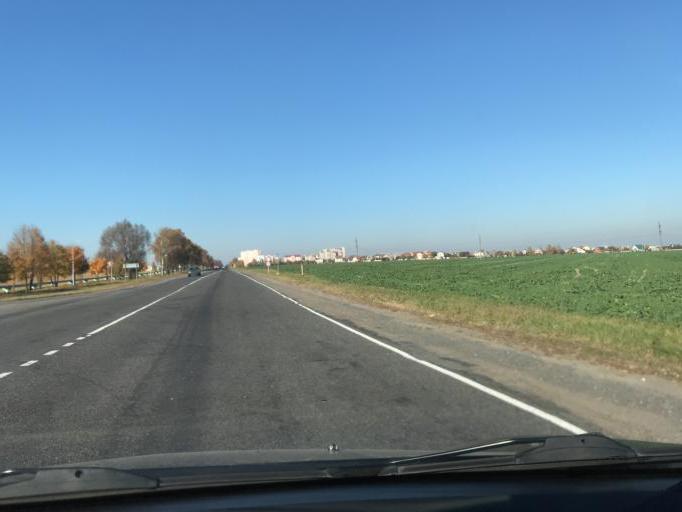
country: BY
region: Gomel
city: Kastsyukowka
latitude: 52.4557
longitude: 30.8207
